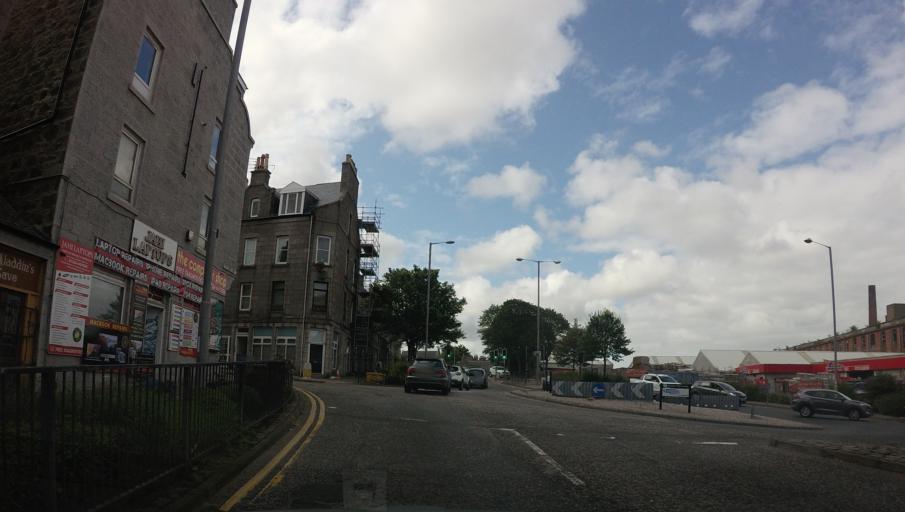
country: GB
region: Scotland
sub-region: Aberdeen City
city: Aberdeen
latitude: 57.1513
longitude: -2.1088
